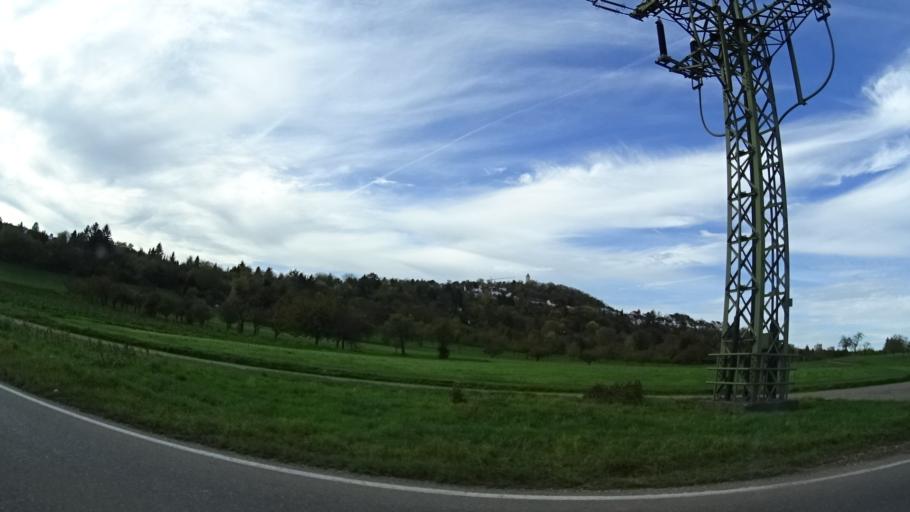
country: DE
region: Baden-Wuerttemberg
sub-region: Regierungsbezirk Stuttgart
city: Leonberg
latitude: 48.8071
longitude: 9.0356
